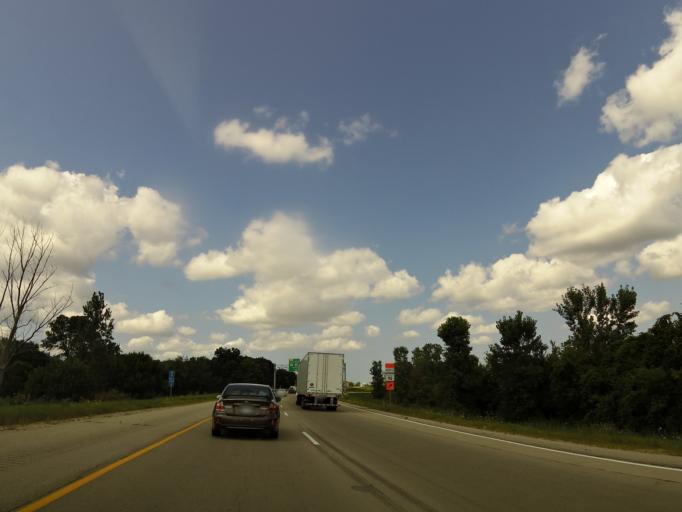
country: US
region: Wisconsin
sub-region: Dane County
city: McFarland
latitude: 43.0417
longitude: -89.2752
